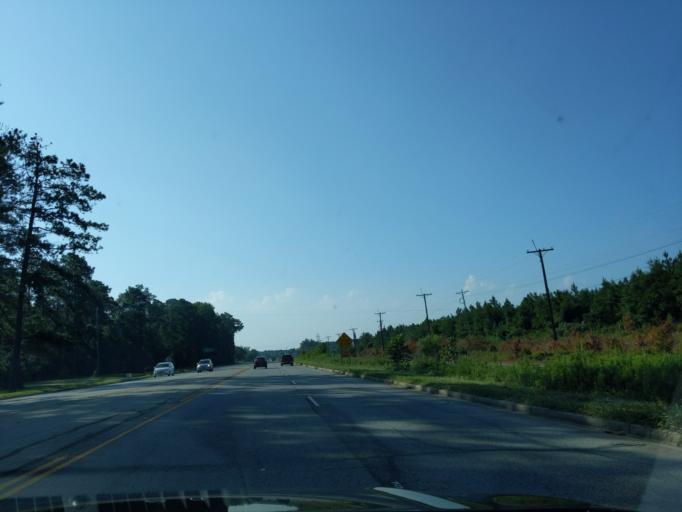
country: US
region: South Carolina
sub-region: Newberry County
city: Prosperity
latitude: 34.2392
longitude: -81.5640
